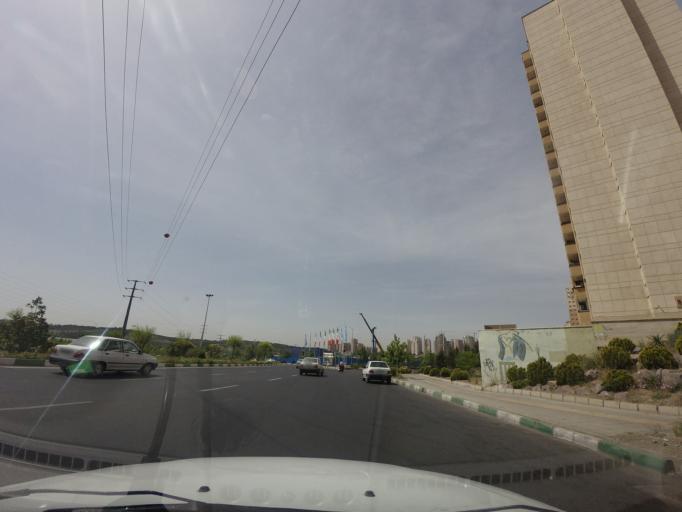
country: IR
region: Tehran
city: Shahr-e Qods
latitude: 35.7540
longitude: 51.2084
